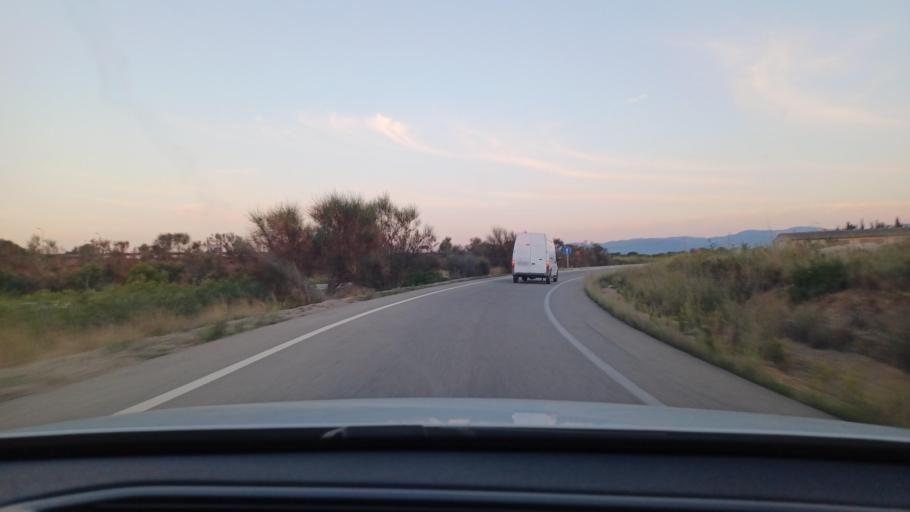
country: ES
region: Catalonia
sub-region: Provincia de Tarragona
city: Alcanar
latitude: 40.5463
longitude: 0.4364
